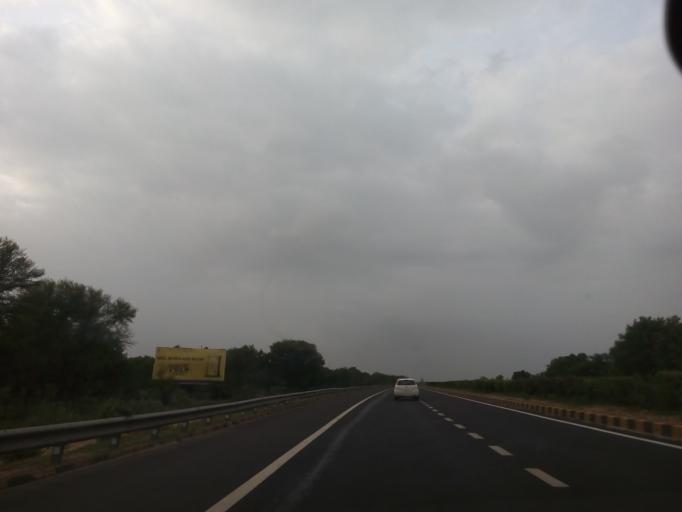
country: IN
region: Gujarat
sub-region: Kheda
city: Mahemdavad
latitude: 22.8779
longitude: 72.7983
